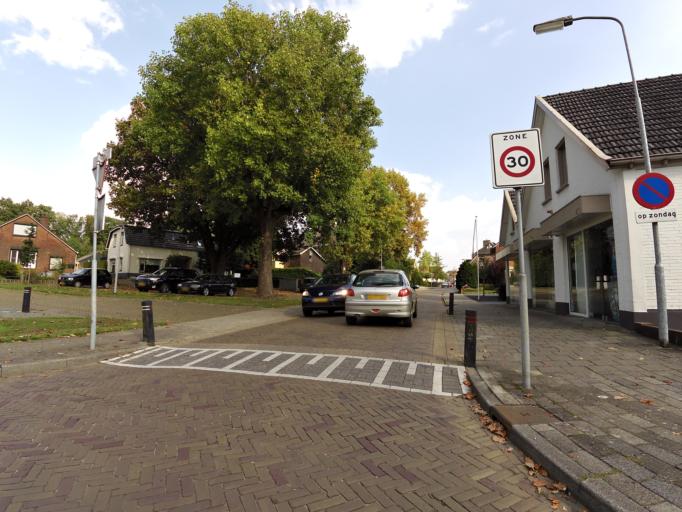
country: NL
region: Gelderland
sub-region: Gemeente Aalten
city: Aalten
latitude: 51.9268
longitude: 6.5752
